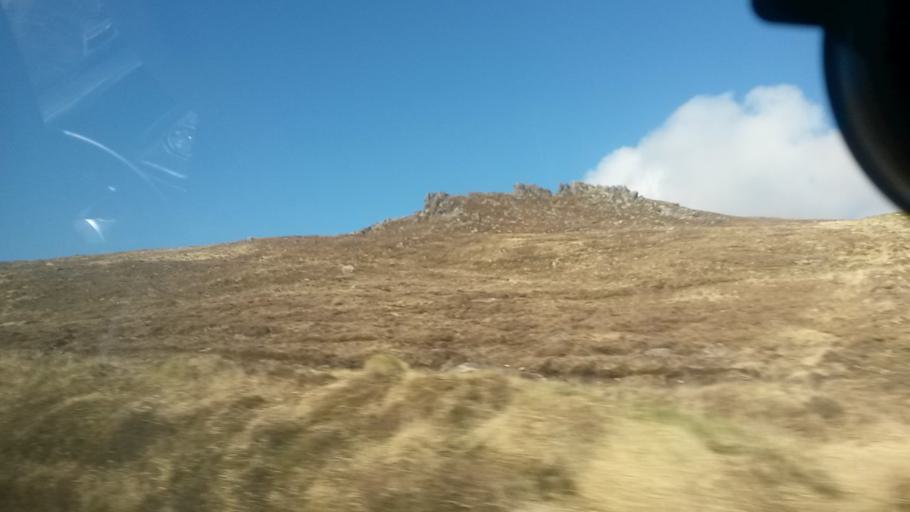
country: IE
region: Munster
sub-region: Ciarrai
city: Dingle
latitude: 52.1448
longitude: -10.4639
